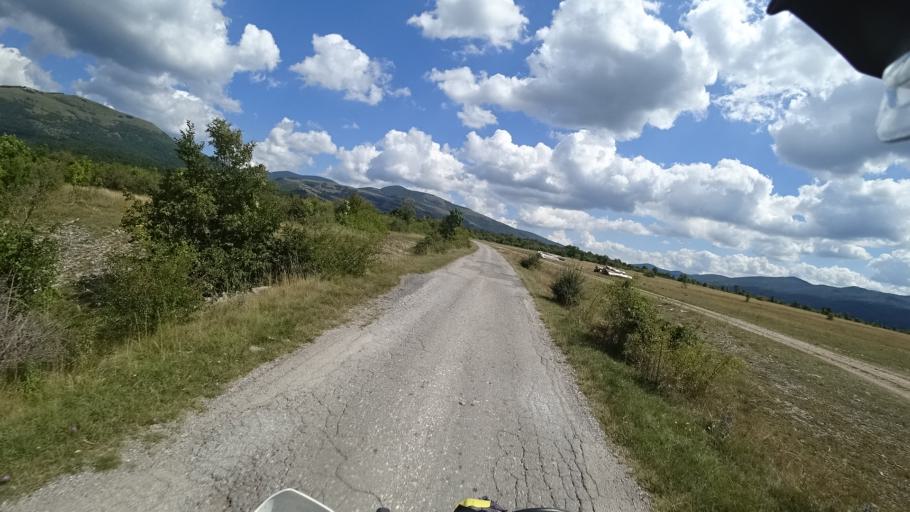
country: HR
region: Zadarska
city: Gracac
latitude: 44.5433
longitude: 15.7983
